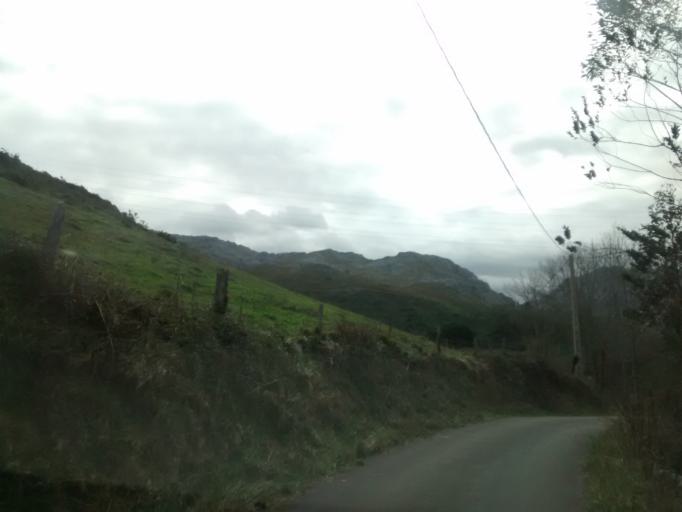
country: ES
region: Cantabria
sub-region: Provincia de Cantabria
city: Lierganes
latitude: 43.3283
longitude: -3.7043
